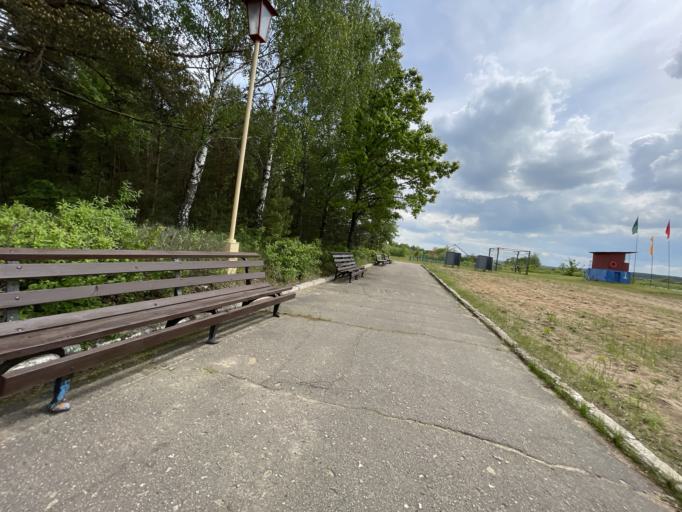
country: BY
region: Minsk
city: Stowbtsy
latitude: 53.4239
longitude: 26.8159
